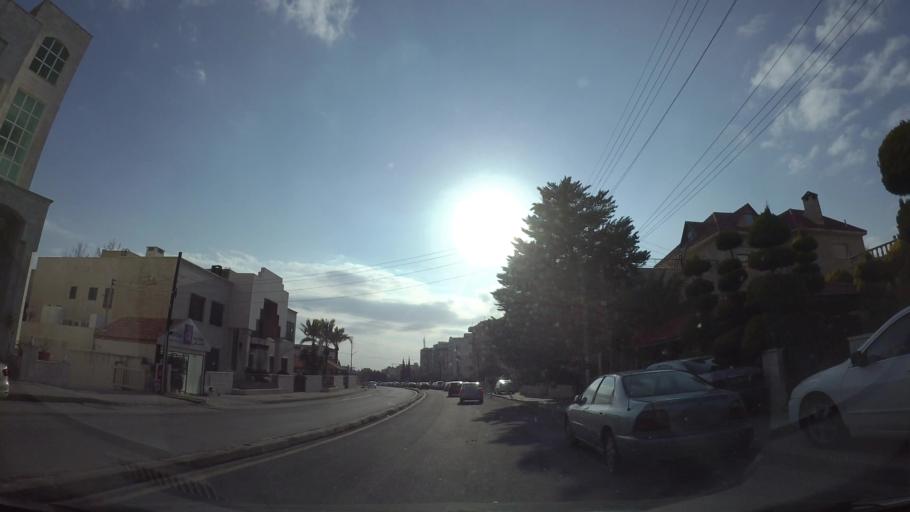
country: JO
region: Amman
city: Al Jubayhah
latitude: 31.9793
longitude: 35.8718
